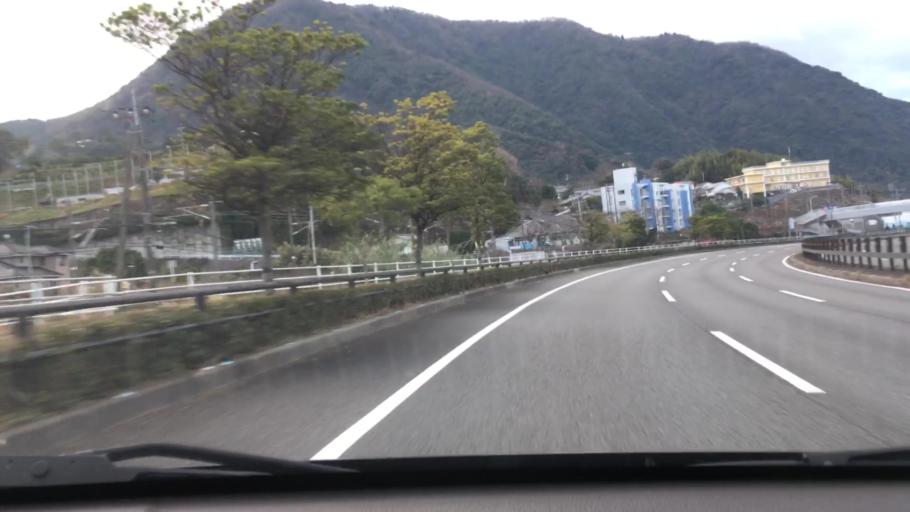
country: JP
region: Oita
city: Beppu
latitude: 33.2551
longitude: 131.5473
